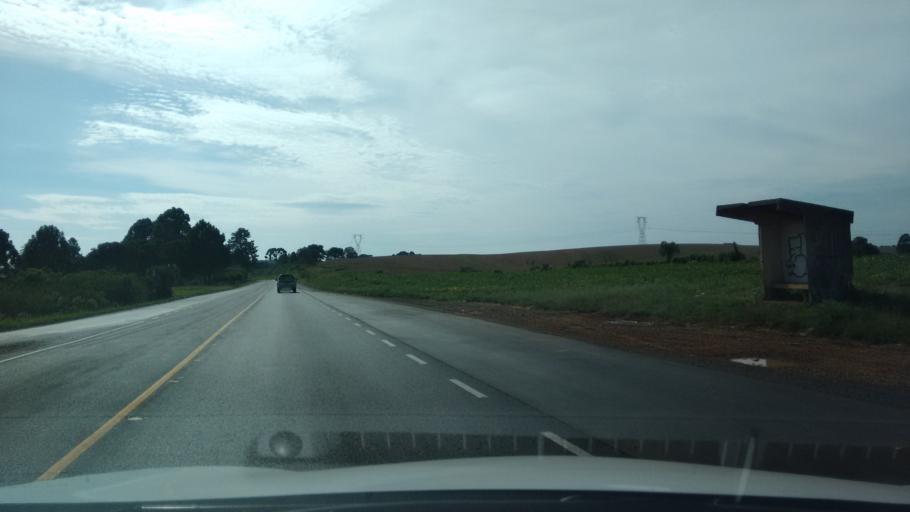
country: BR
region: Santa Catarina
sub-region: Campos Novos
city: Campos Novos
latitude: -27.3354
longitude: -50.9599
